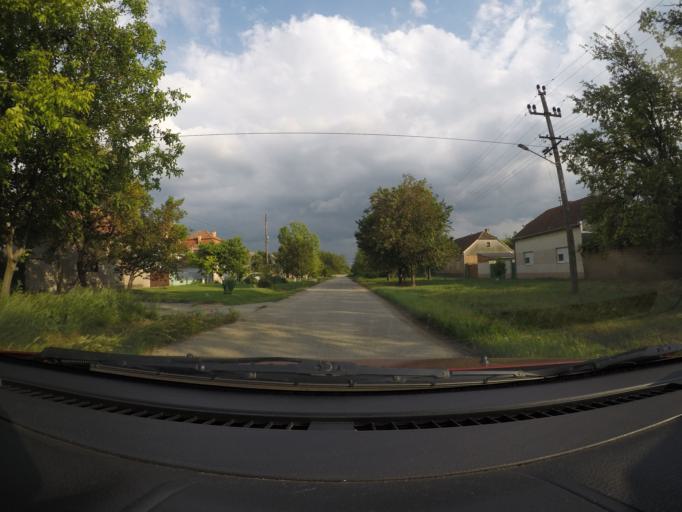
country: RS
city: Debeljaca
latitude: 45.0655
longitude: 20.6004
